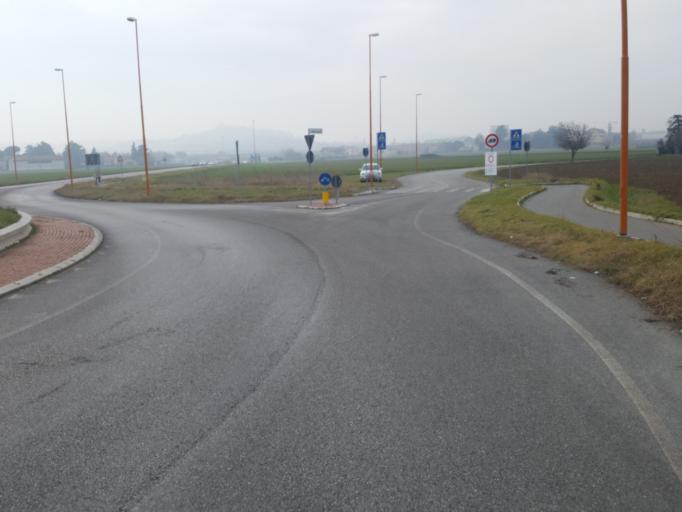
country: IT
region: Emilia-Romagna
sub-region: Forli-Cesena
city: Cesena
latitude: 44.1498
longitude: 12.2695
